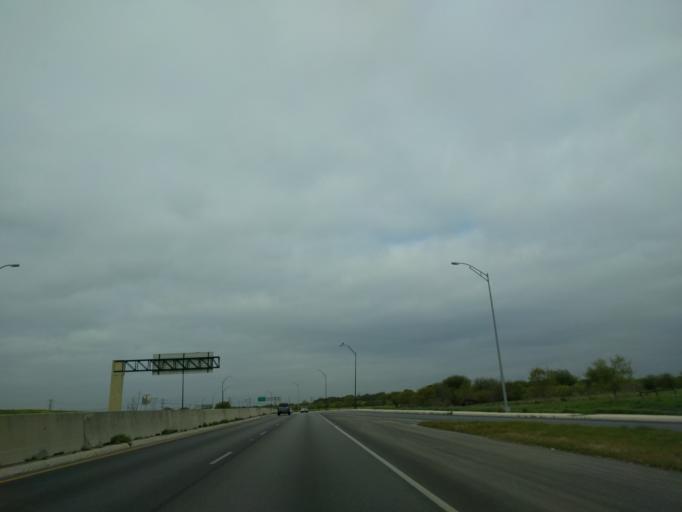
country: US
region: Texas
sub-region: Bexar County
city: Alamo Heights
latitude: 29.5468
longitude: -98.4404
